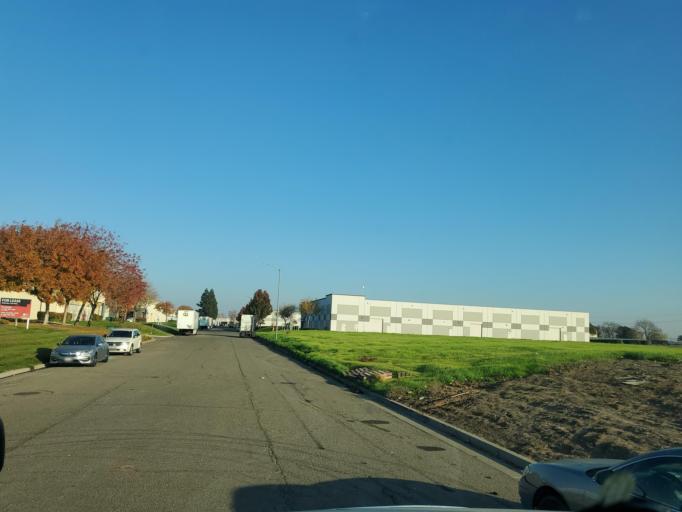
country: US
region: California
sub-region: San Joaquin County
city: Kennedy
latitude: 37.9072
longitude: -121.2181
